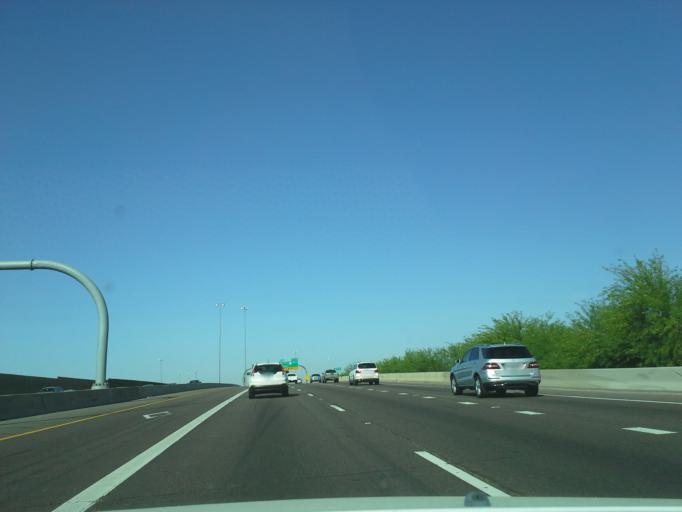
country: US
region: Arizona
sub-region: Maricopa County
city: Phoenix
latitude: 33.4621
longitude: -112.0279
